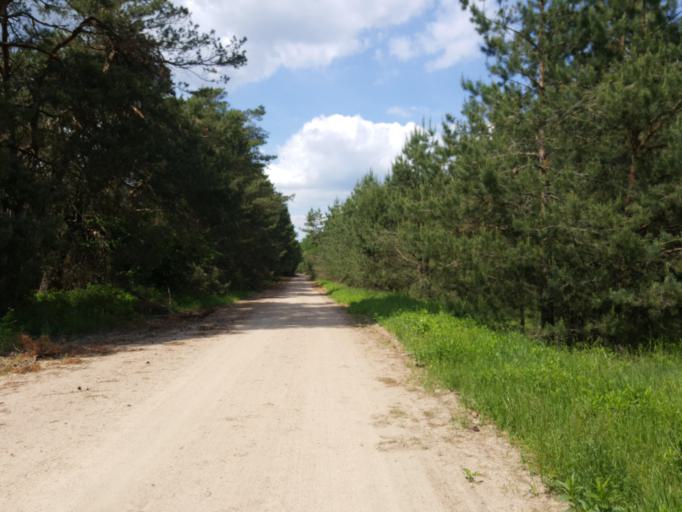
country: BY
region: Brest
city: Kamyanyuki
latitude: 52.5525
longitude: 23.6492
